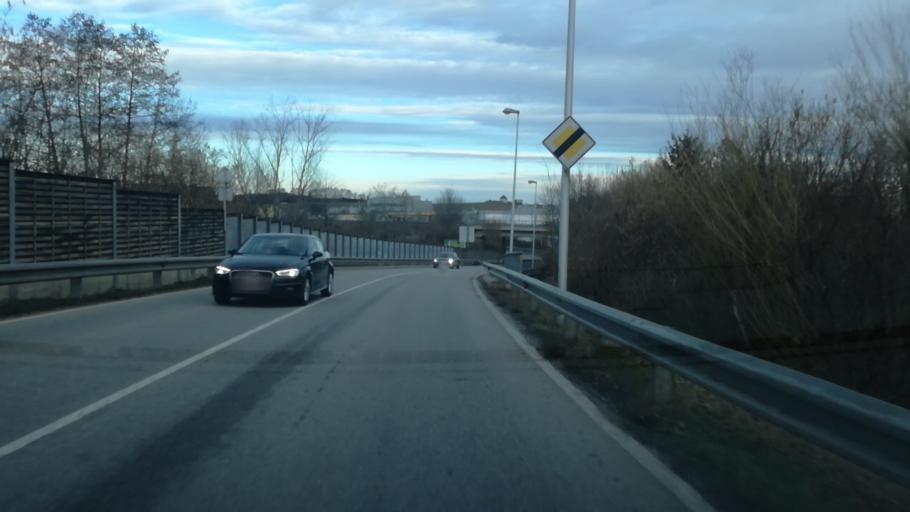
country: AT
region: Upper Austria
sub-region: Politischer Bezirk Ried im Innkreis
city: Ried im Innkreis
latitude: 48.1973
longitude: 13.4759
